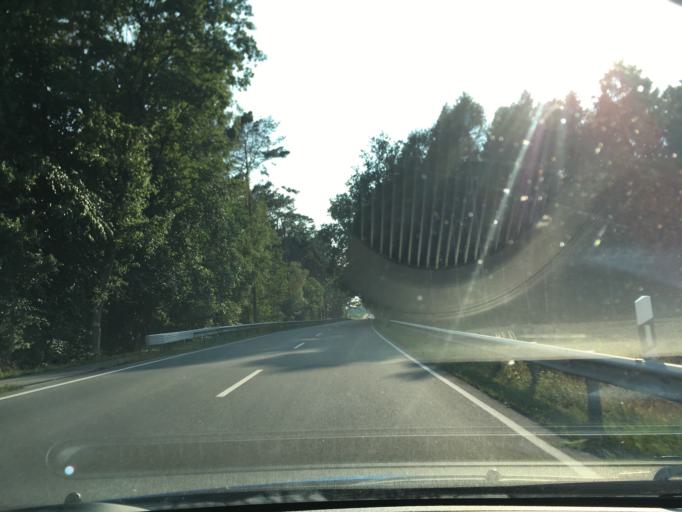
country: DE
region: Lower Saxony
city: Zernien
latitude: 53.0596
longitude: 10.8431
